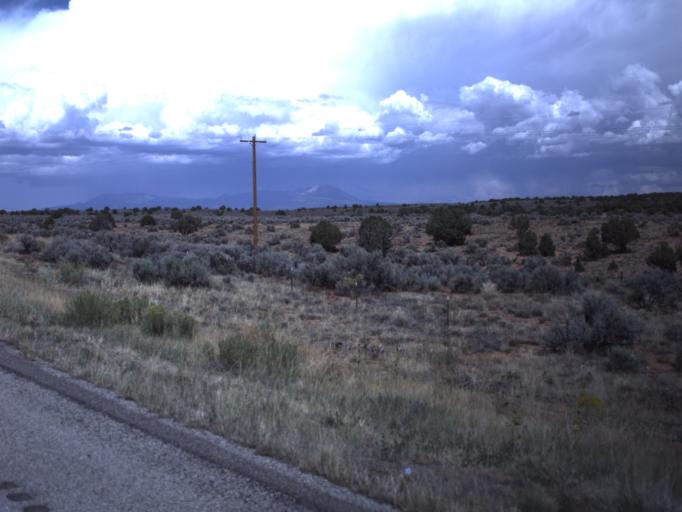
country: US
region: Utah
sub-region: San Juan County
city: Blanding
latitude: 37.4899
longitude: -109.4786
